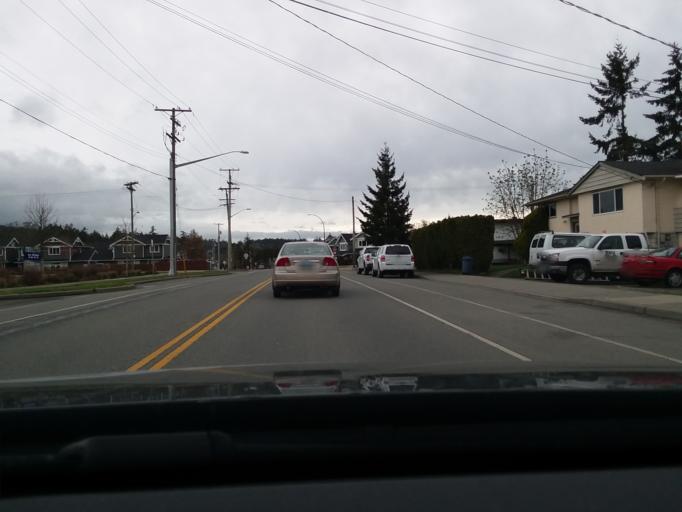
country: CA
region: British Columbia
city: North Saanich
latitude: 48.6654
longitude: -123.4168
